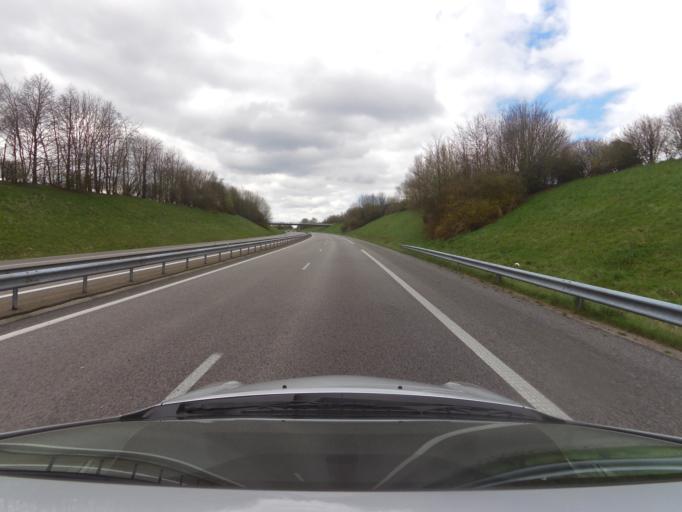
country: FR
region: Haute-Normandie
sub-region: Departement de la Seine-Maritime
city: Saint-Romain-de-Colbosc
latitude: 49.5702
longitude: 0.3558
